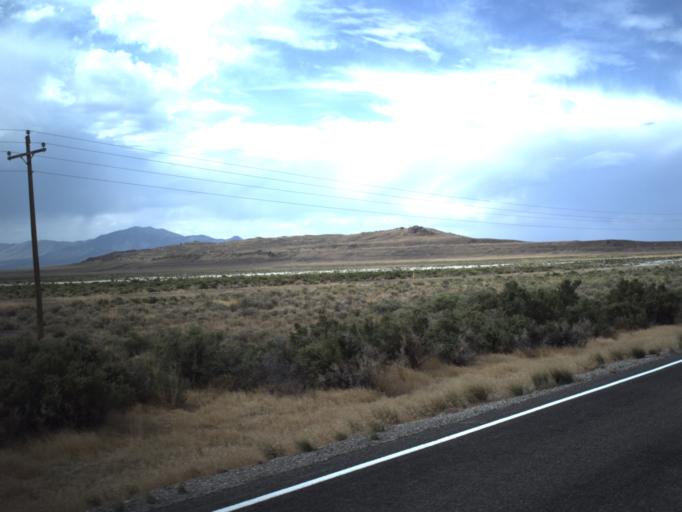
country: US
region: Utah
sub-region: Tooele County
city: Wendover
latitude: 41.4225
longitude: -113.8802
